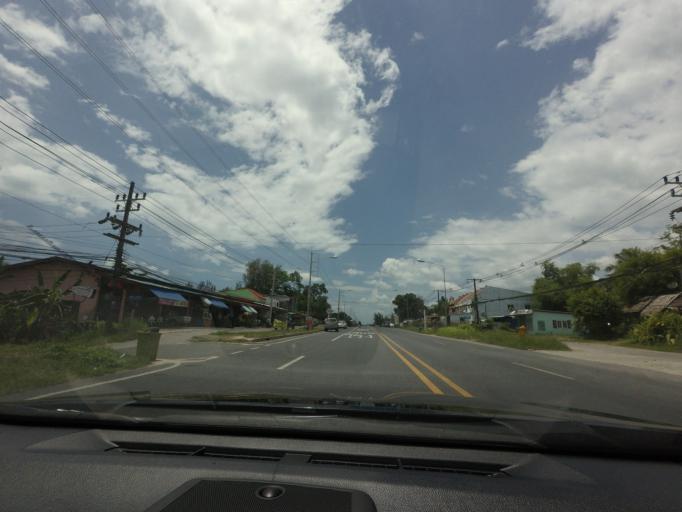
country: TH
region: Phangnga
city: Ban Khao Lak
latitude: 8.6557
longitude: 98.2535
